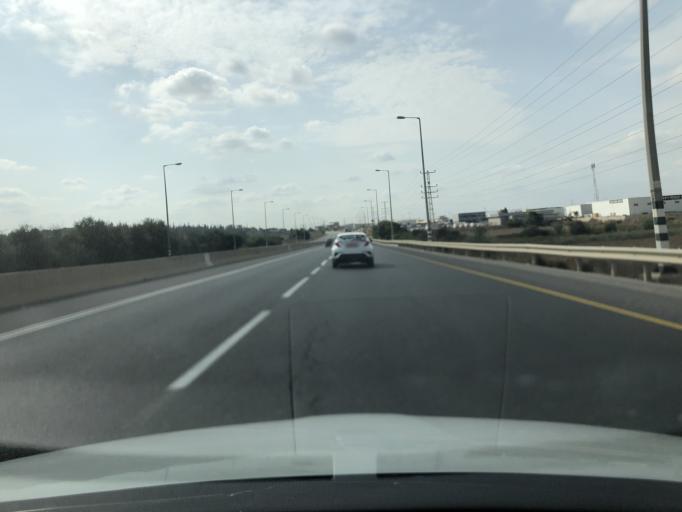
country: IL
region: Central District
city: Tirah
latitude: 32.2306
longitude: 34.9835
